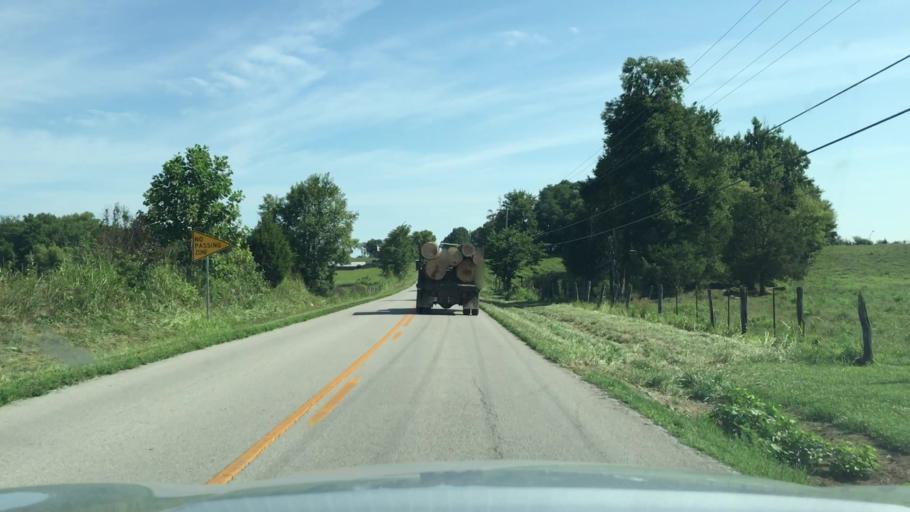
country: US
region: Kentucky
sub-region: Clinton County
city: Albany
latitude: 36.7612
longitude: -84.9973
